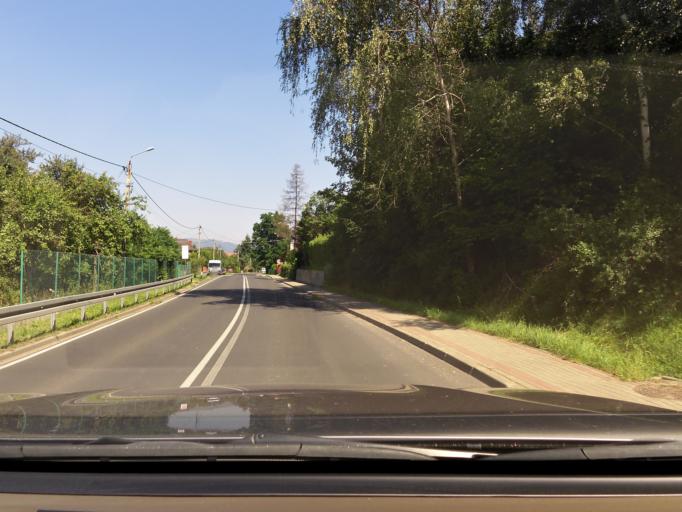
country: PL
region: Silesian Voivodeship
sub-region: Powiat zywiecki
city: Rajcza
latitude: 49.5268
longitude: 19.1116
